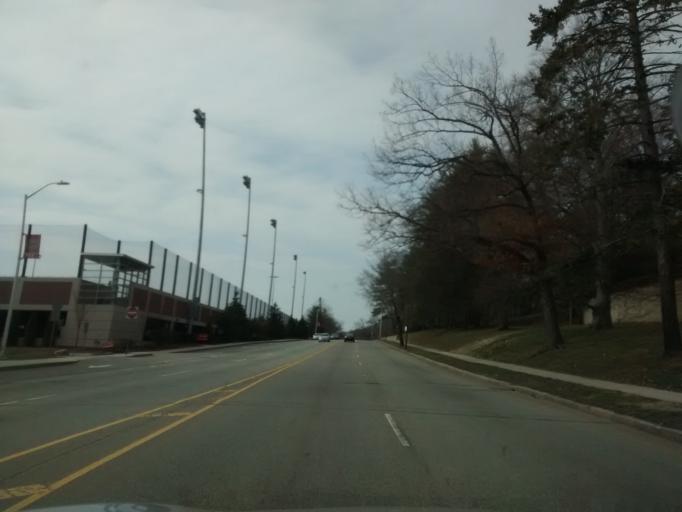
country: US
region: Massachusetts
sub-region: Worcester County
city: Worcester
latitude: 42.2770
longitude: -71.8100
